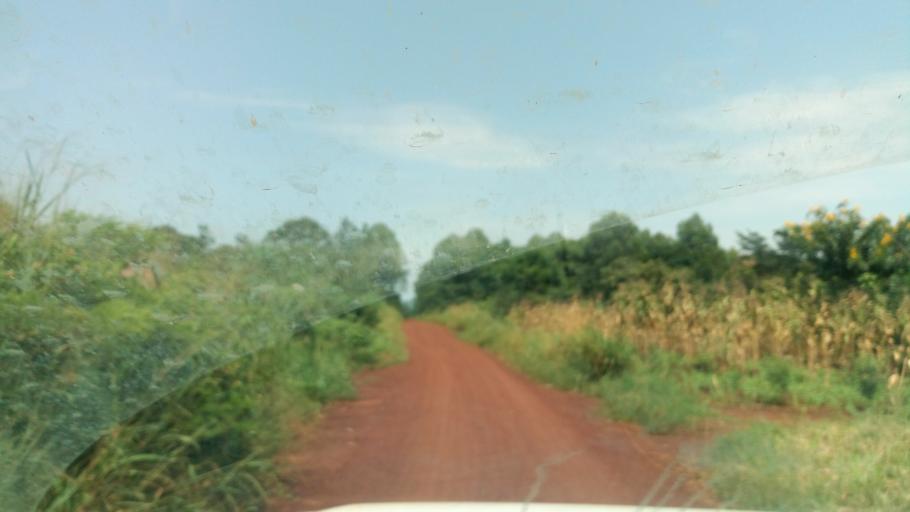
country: UG
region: Western Region
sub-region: Masindi District
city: Masindi
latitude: 1.6677
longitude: 31.8198
